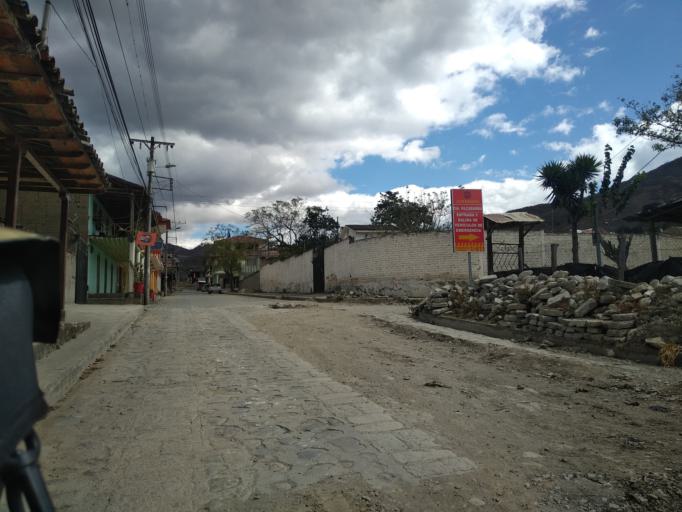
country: EC
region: Loja
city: Loja
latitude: -4.2590
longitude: -79.2220
